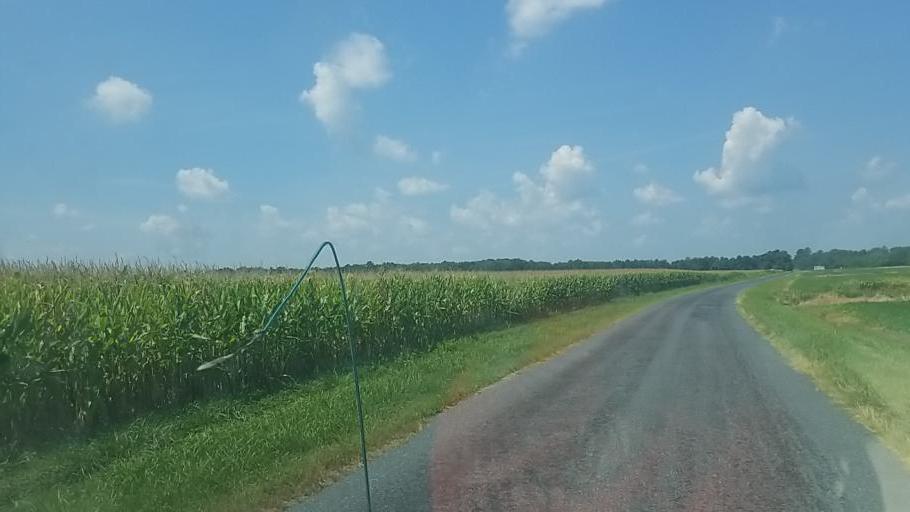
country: US
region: Maryland
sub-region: Worcester County
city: Berlin
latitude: 38.2978
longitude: -75.2752
